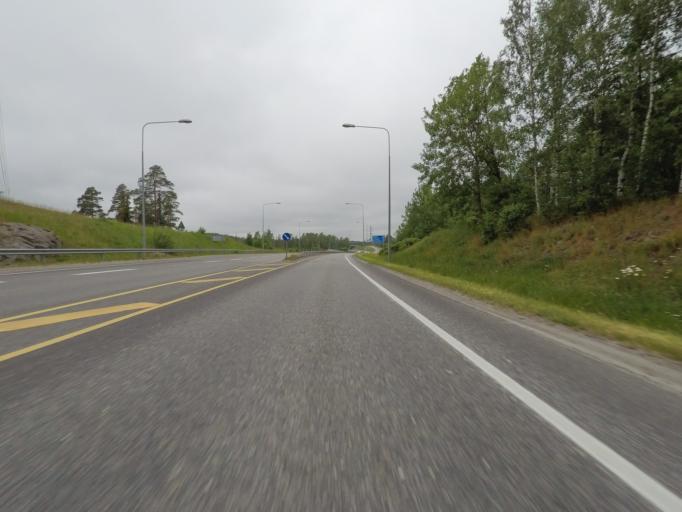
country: FI
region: Varsinais-Suomi
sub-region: Turku
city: Naantali
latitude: 60.4711
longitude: 22.0749
